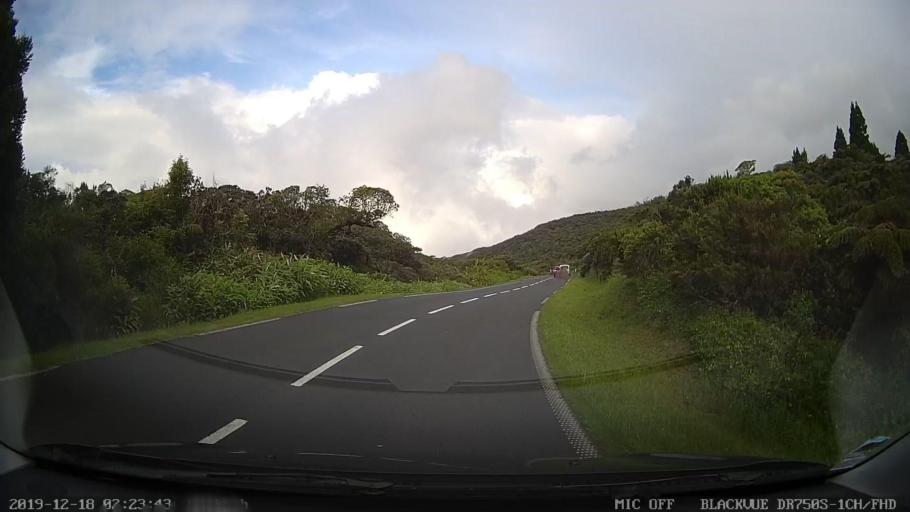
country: RE
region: Reunion
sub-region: Reunion
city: Cilaos
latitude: -21.1642
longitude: 55.5896
